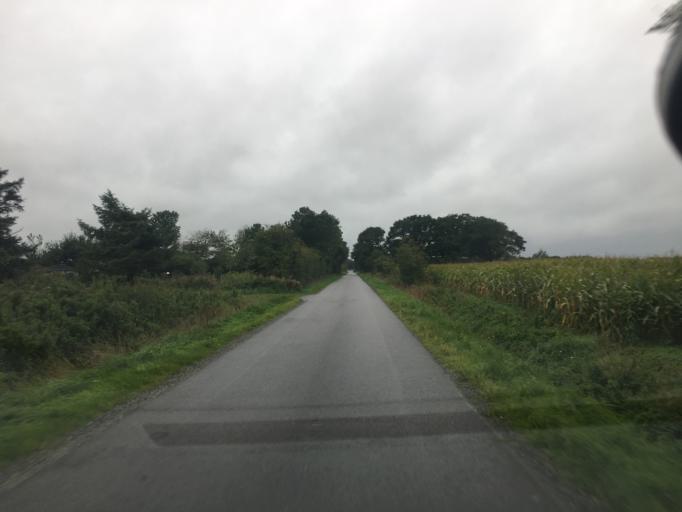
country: DE
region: Schleswig-Holstein
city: Ellhoft
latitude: 54.9397
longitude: 8.9791
